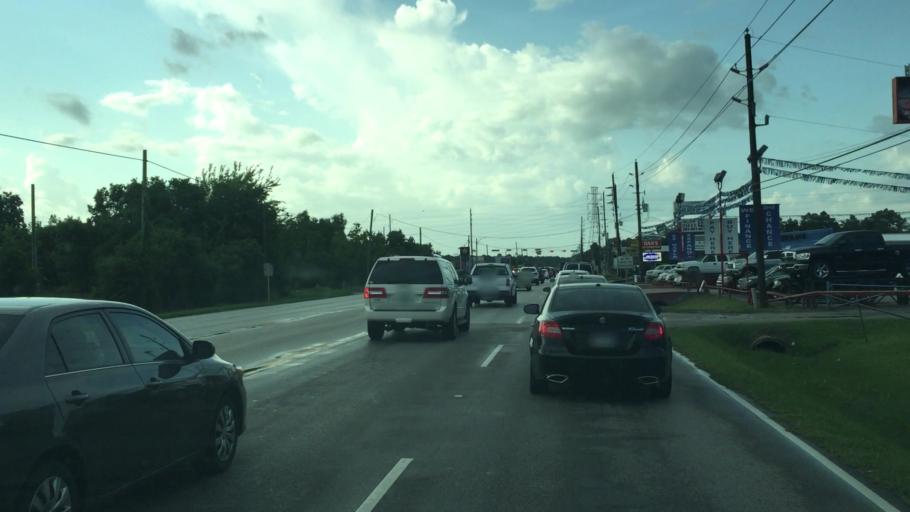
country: US
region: Texas
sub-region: Harris County
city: Spring
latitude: 30.0484
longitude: -95.4918
